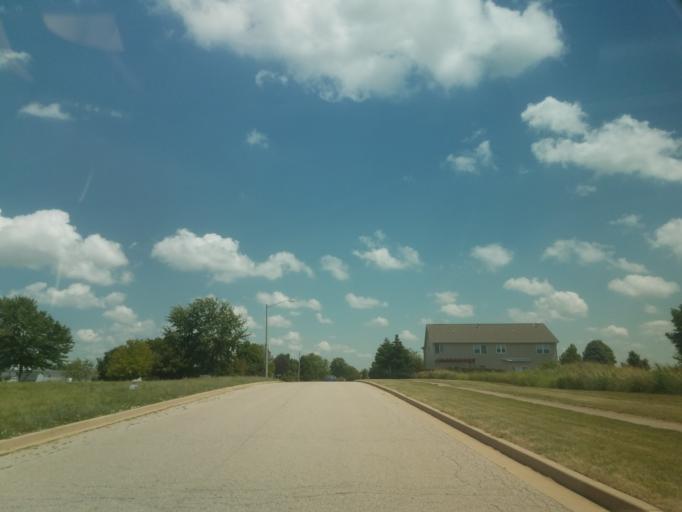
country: US
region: Illinois
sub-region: McLean County
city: Bloomington
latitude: 40.4428
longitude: -89.0355
